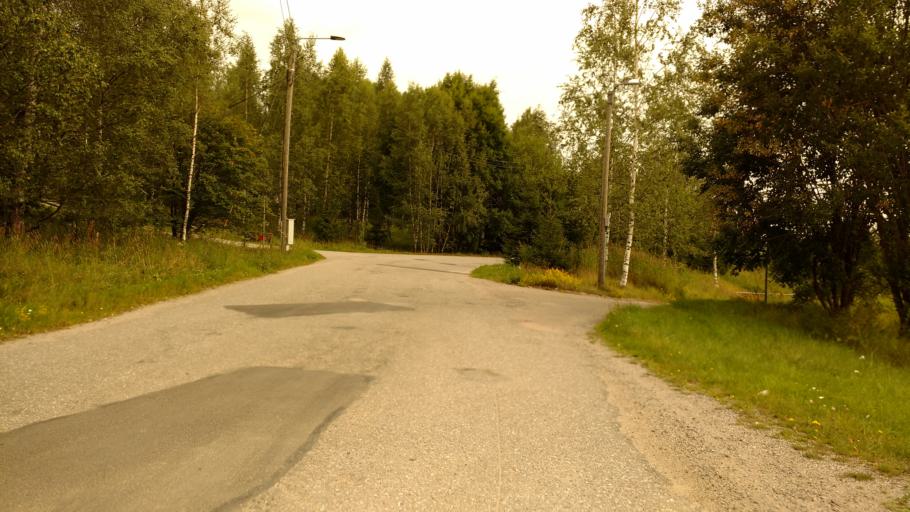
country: FI
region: Varsinais-Suomi
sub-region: Turku
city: Piikkioe
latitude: 60.4306
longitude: 22.5414
